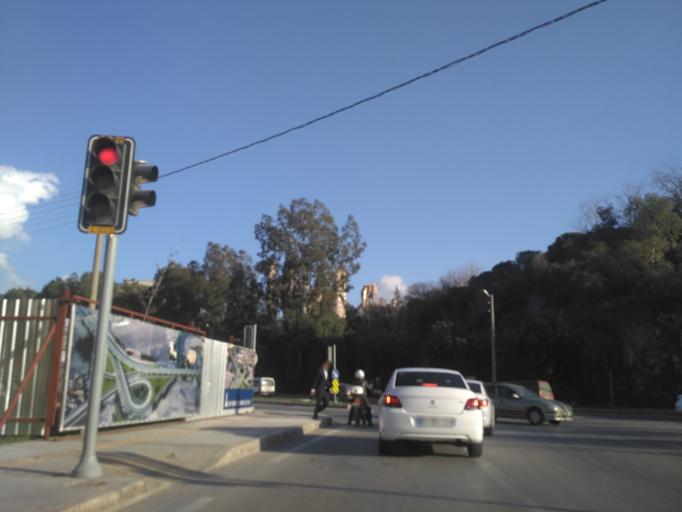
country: TR
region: Izmir
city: Buca
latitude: 38.4275
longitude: 27.2118
